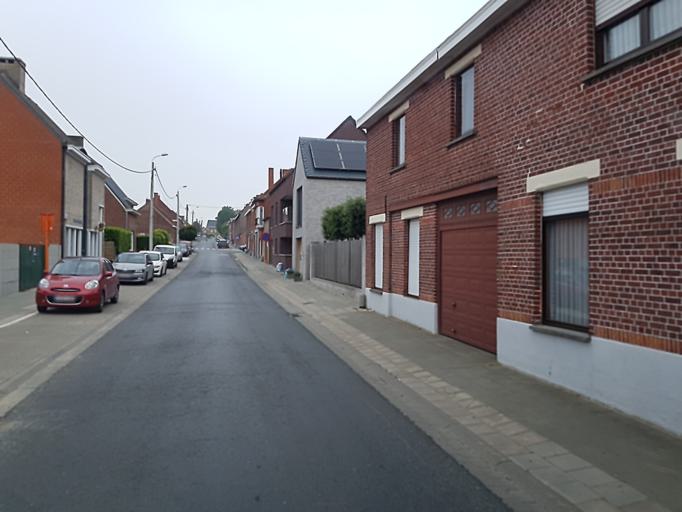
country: BE
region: Flanders
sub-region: Provincie West-Vlaanderen
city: Moorslede
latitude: 50.8924
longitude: 3.0601
